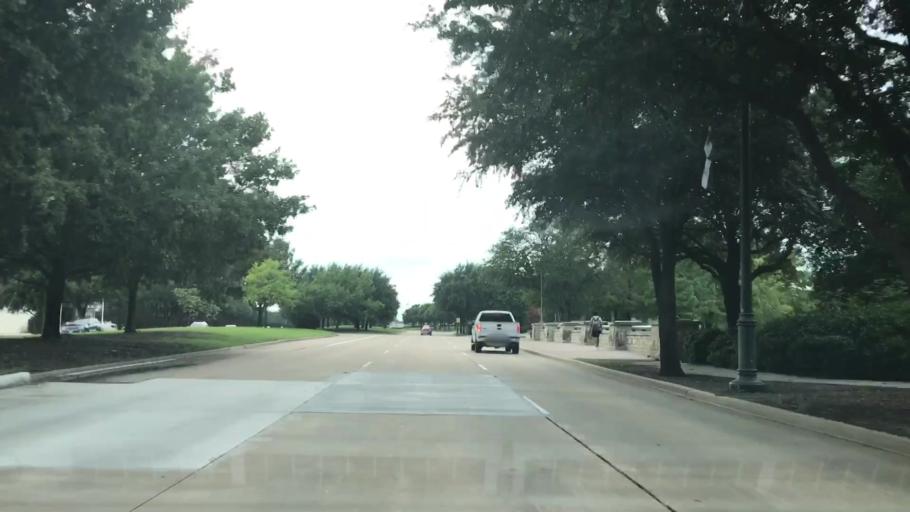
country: US
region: Texas
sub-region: Collin County
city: Frisco
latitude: 33.1089
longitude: -96.8110
